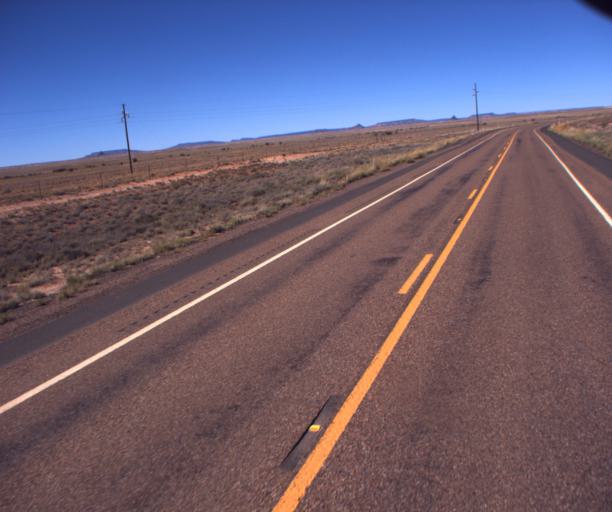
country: US
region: Arizona
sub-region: Navajo County
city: Holbrook
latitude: 35.0668
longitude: -110.0993
